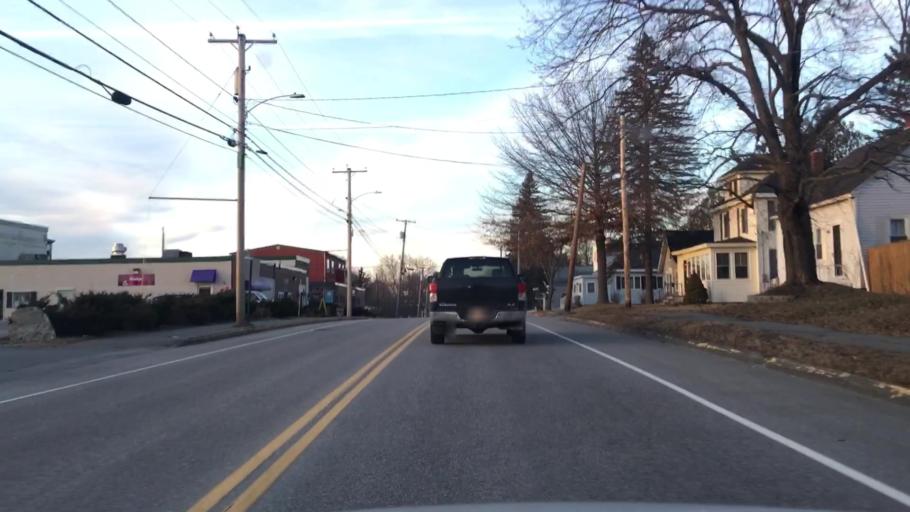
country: US
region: Maine
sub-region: Penobscot County
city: Brewer
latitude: 44.7905
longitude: -68.7565
